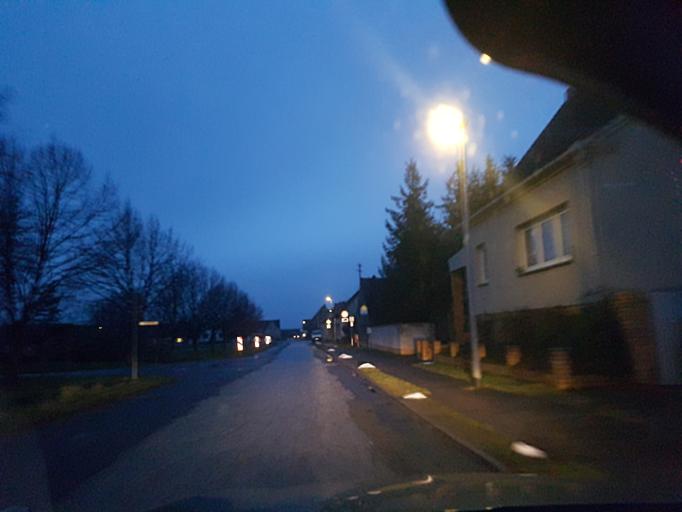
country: DE
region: Brandenburg
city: Doberlug-Kirchhain
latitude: 51.6125
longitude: 13.5895
